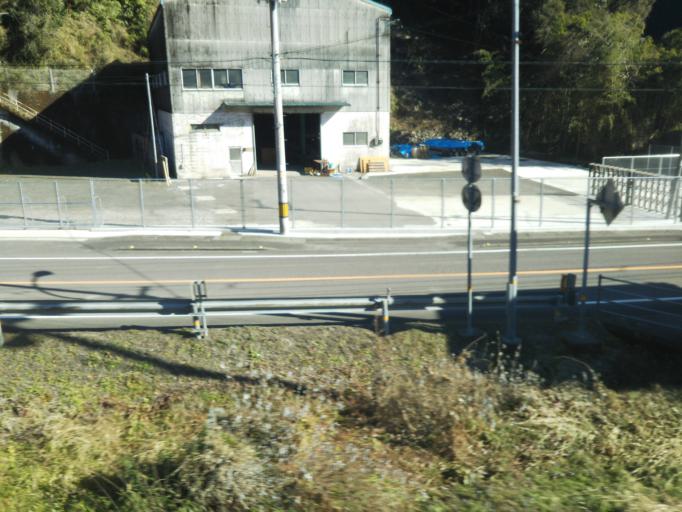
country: JP
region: Kochi
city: Nakamura
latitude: 33.1075
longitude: 133.0988
